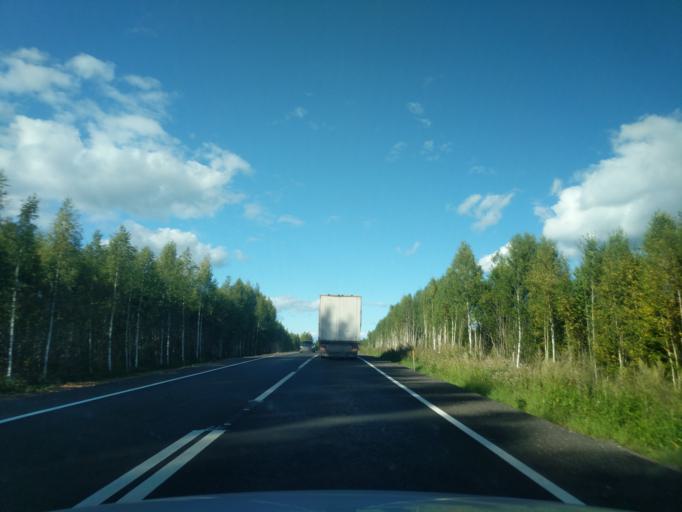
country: RU
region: Kostroma
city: Makar'yev
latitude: 57.9928
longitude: 43.9692
